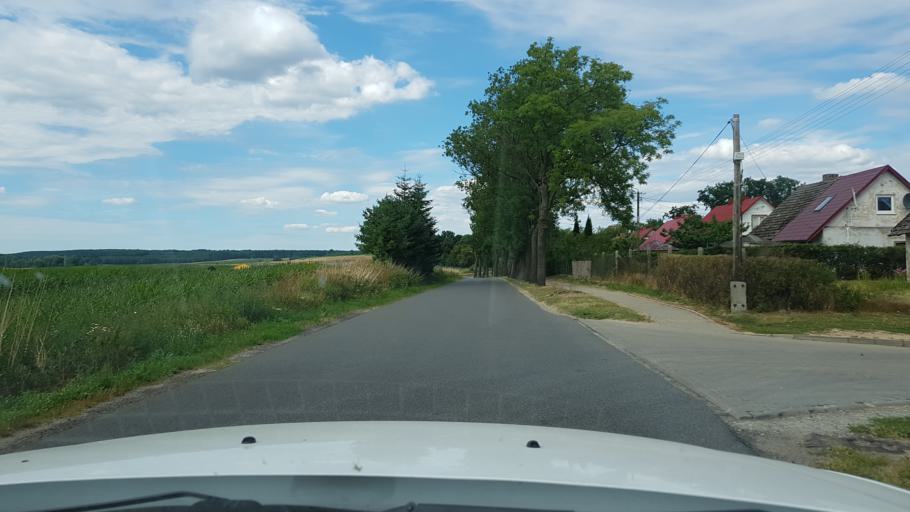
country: PL
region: West Pomeranian Voivodeship
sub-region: Powiat drawski
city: Kalisz Pomorski
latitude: 53.3334
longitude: 15.9314
